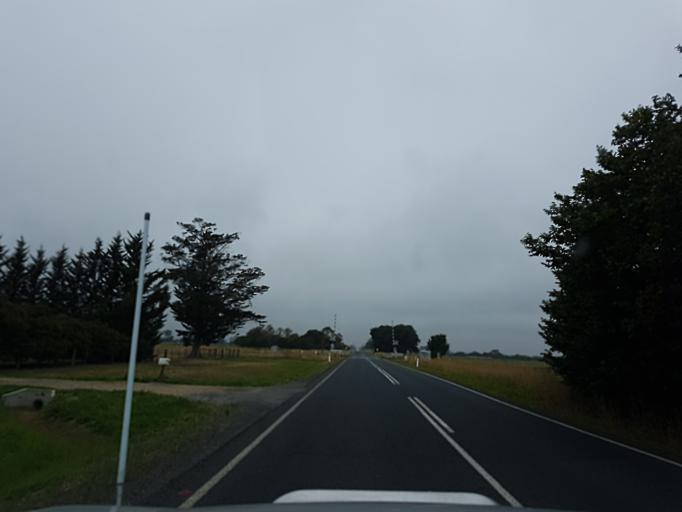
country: AU
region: Victoria
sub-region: Wellington
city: Sale
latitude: -38.0666
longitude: 147.0629
